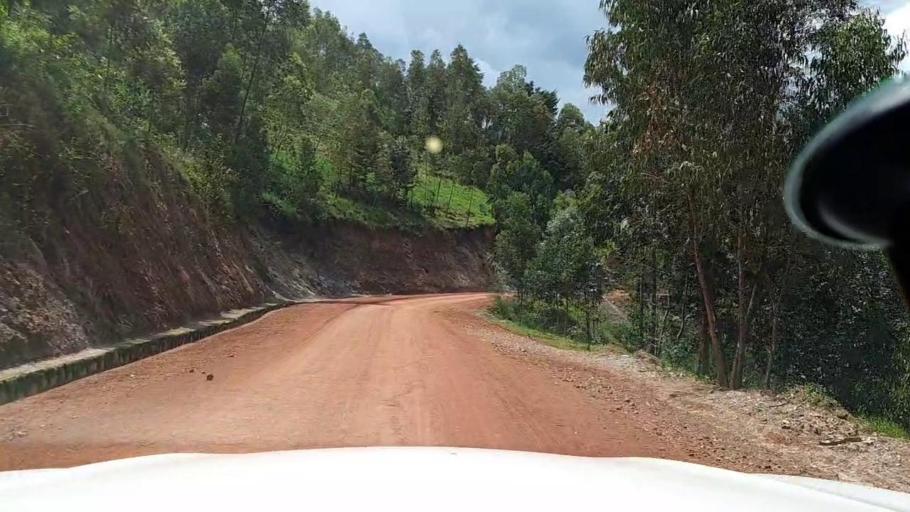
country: RW
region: Northern Province
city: Byumba
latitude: -1.7548
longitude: 29.8493
